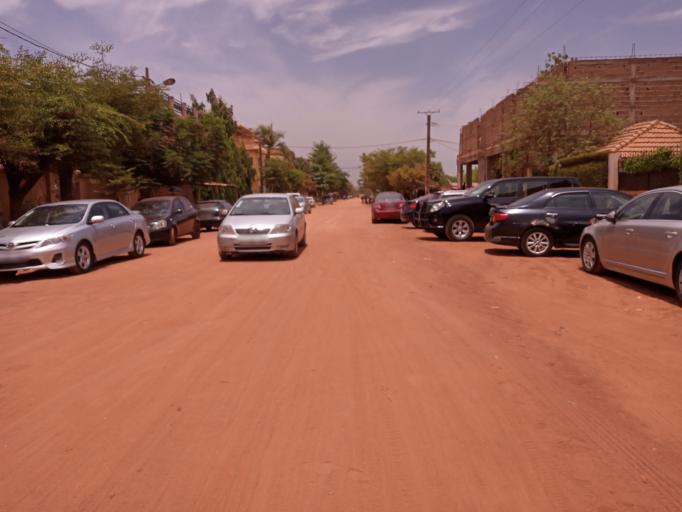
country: ML
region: Bamako
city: Bamako
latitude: 12.5853
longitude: -7.9548
